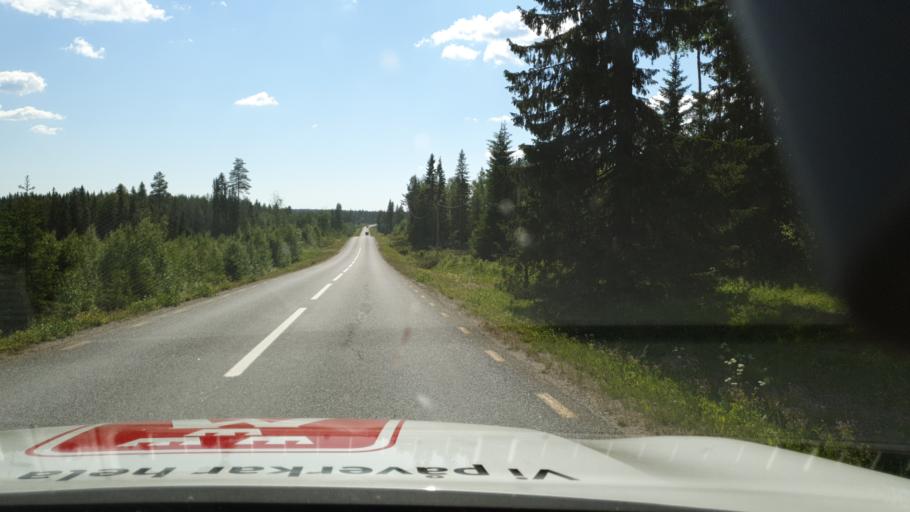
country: SE
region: Vaesterbotten
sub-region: Skelleftea Kommun
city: Burtraesk
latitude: 64.3924
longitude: 20.2928
